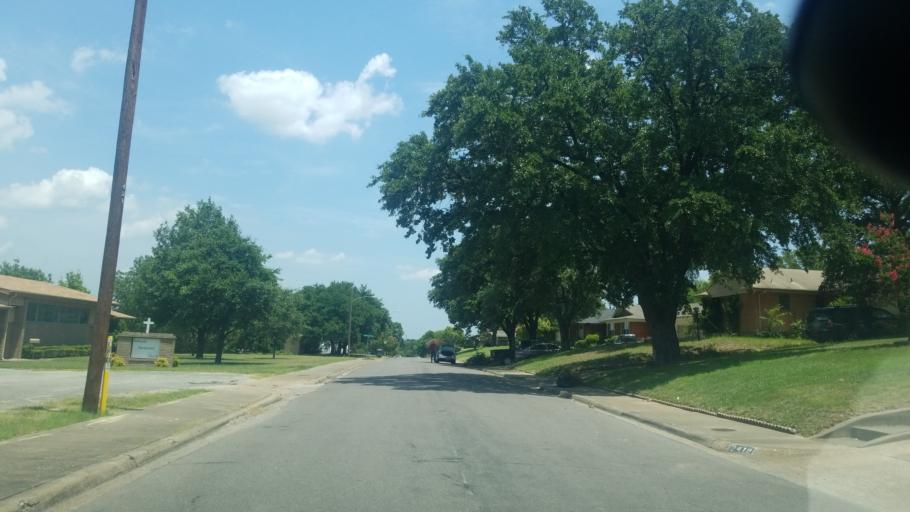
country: US
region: Texas
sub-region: Dallas County
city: Dallas
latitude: 32.7213
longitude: -96.7832
